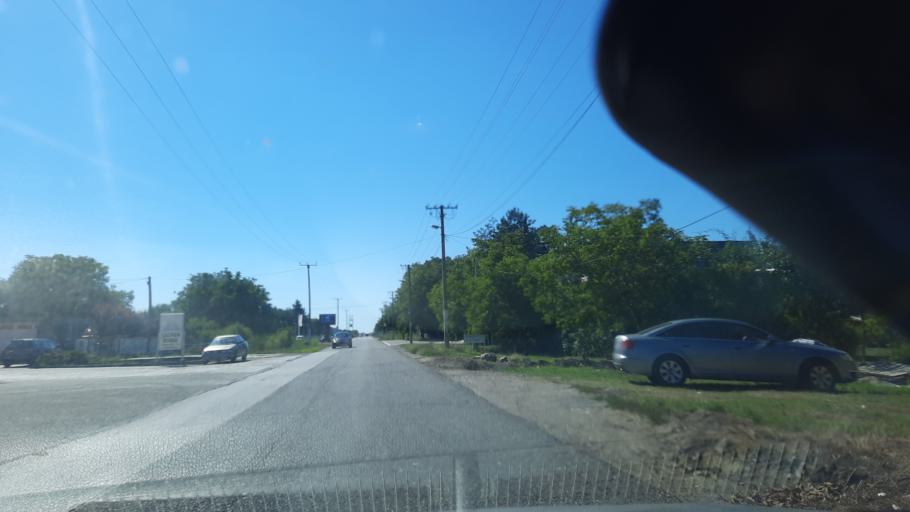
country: RS
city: Simanovci
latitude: 44.8765
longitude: 20.0757
